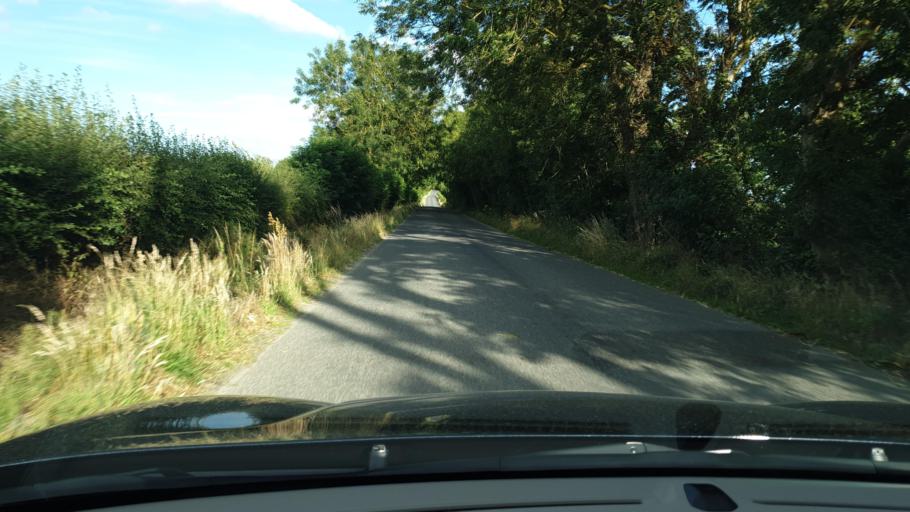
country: IE
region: Leinster
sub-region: An Mhi
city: Stamullin
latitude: 53.6235
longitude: -6.3397
